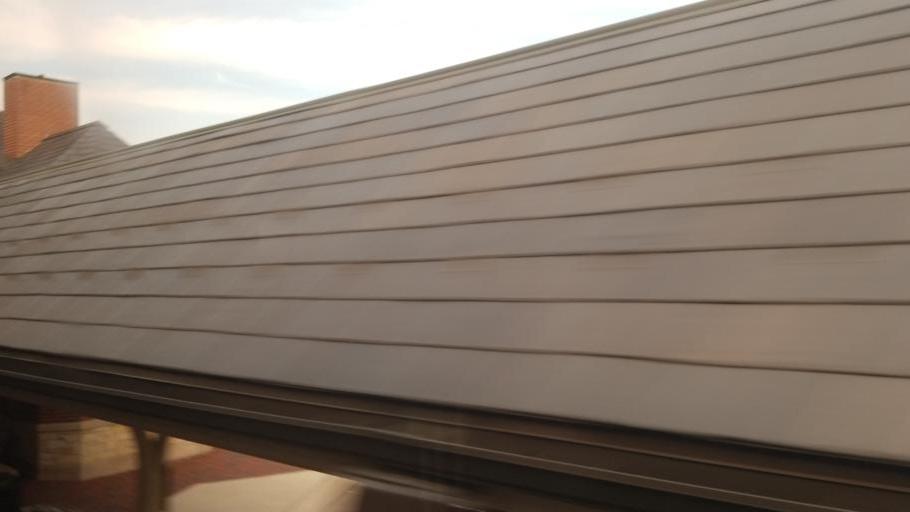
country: US
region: Illinois
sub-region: Cook County
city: Western Springs
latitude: 41.8090
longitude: -87.9015
